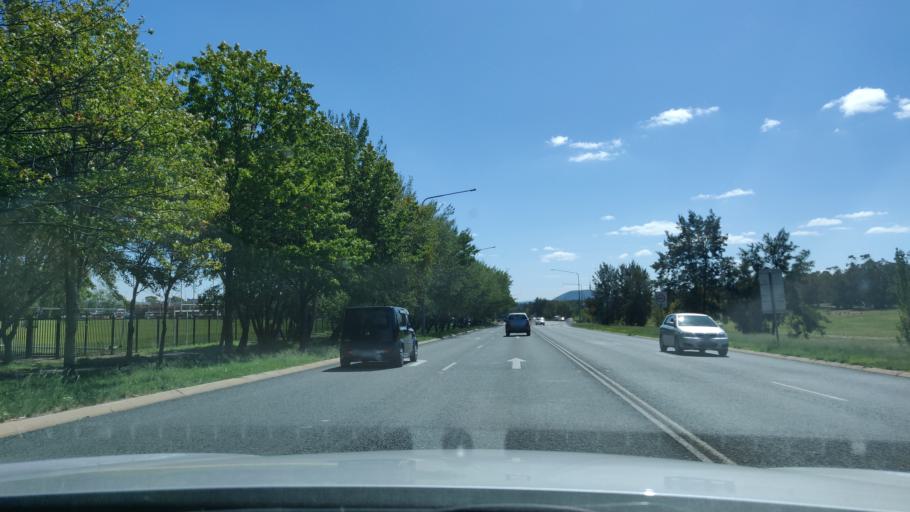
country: AU
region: Australian Capital Territory
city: Forrest
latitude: -35.3596
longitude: 149.0916
